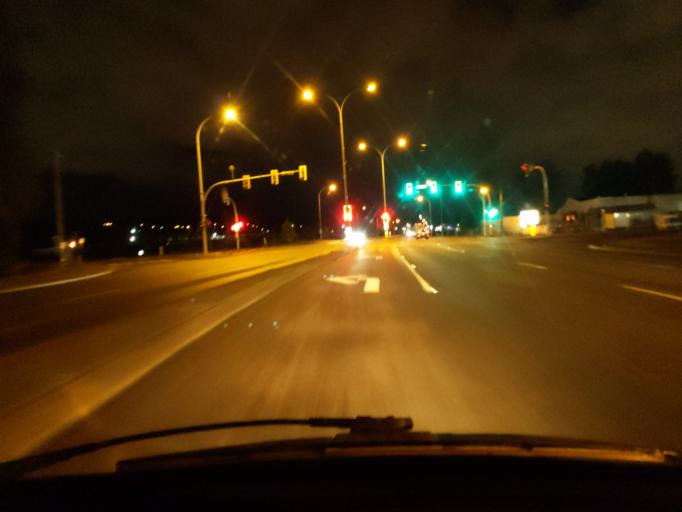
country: CA
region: British Columbia
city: New Westminster
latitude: 49.1997
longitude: -122.8820
